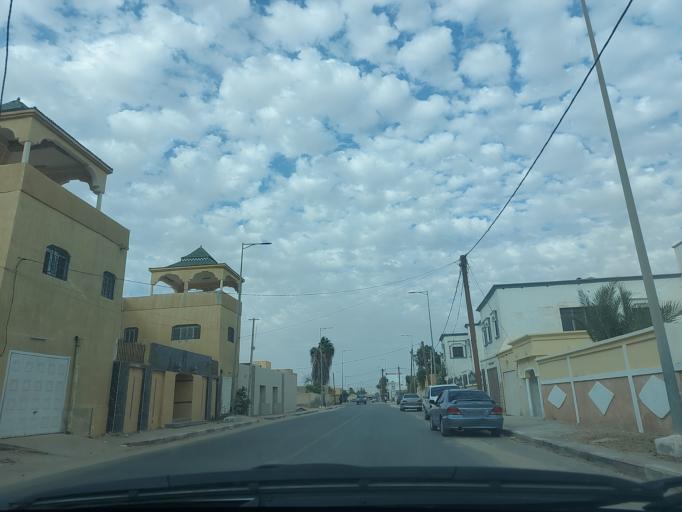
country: MR
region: Nouakchott
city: Nouakchott
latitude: 18.1083
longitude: -15.9975
